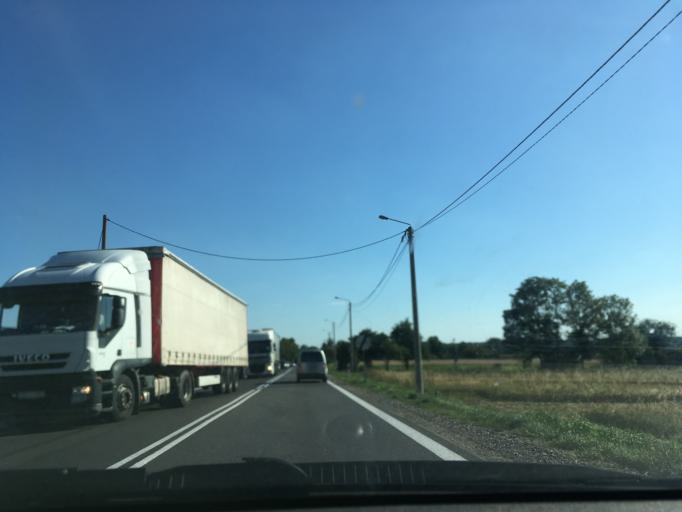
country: PL
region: Podlasie
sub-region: Powiat sokolski
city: Suchowola
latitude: 53.4708
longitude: 23.0902
